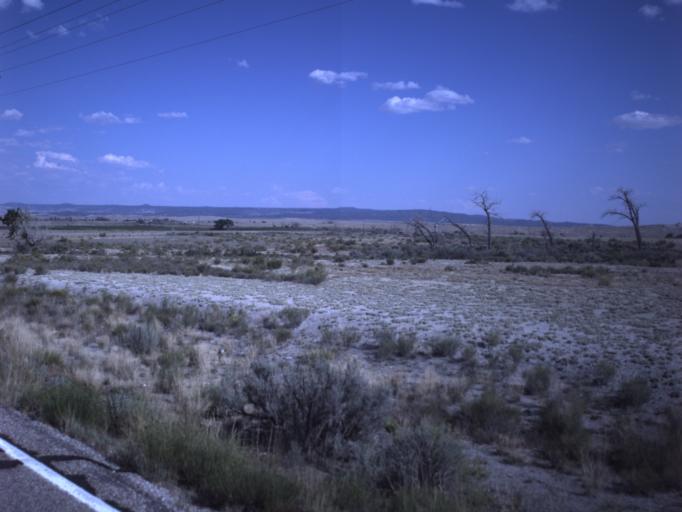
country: US
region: Utah
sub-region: Emery County
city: Huntington
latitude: 39.3449
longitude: -110.9125
